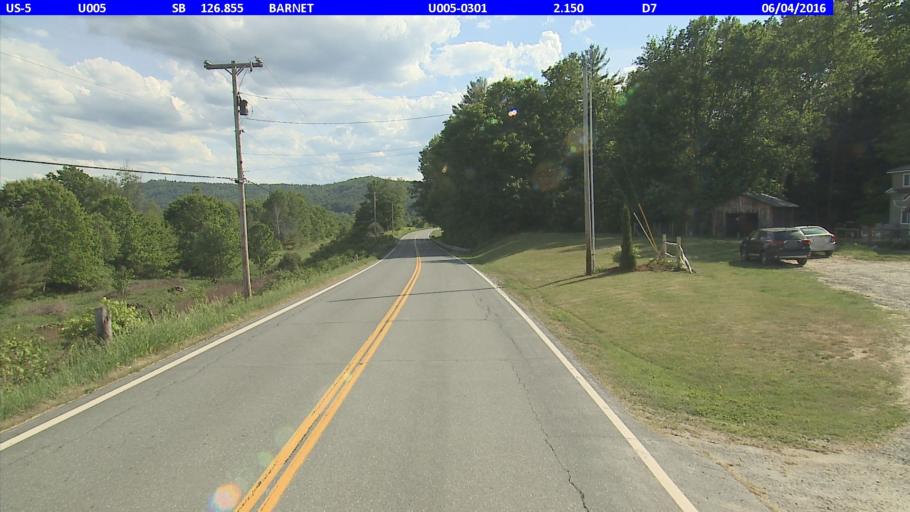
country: US
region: New Hampshire
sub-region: Grafton County
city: Woodsville
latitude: 44.2844
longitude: -72.0615
